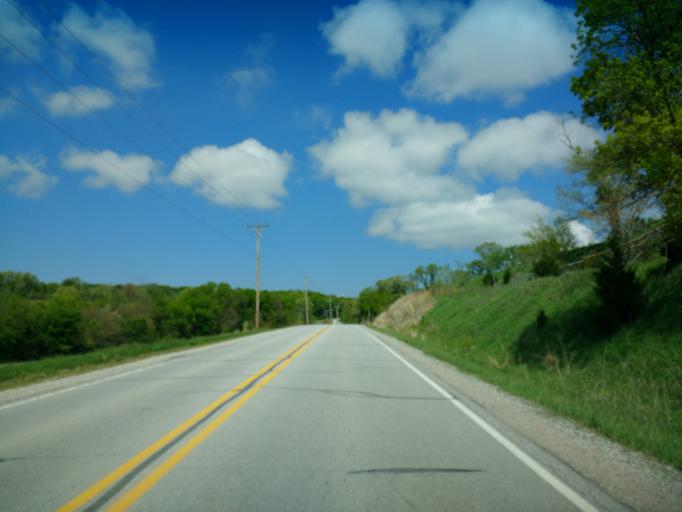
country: US
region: Iowa
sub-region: Pottawattamie County
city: Carter Lake
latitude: 41.4145
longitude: -95.8435
